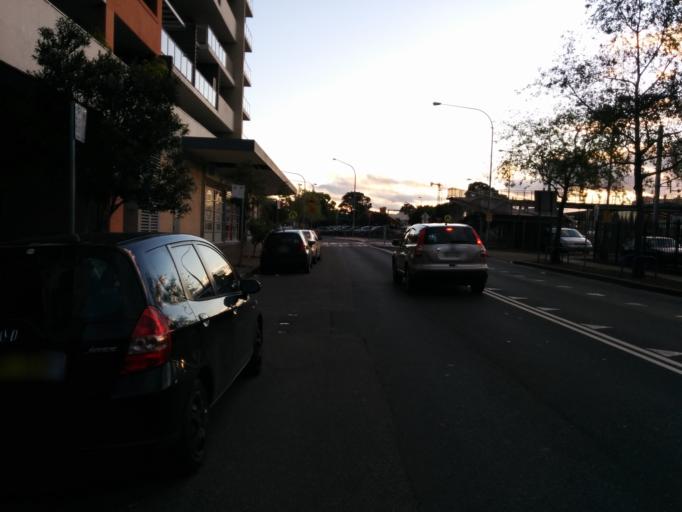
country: AU
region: New South Wales
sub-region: Fairfield
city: Fairfield East
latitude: -33.8715
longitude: 150.9591
